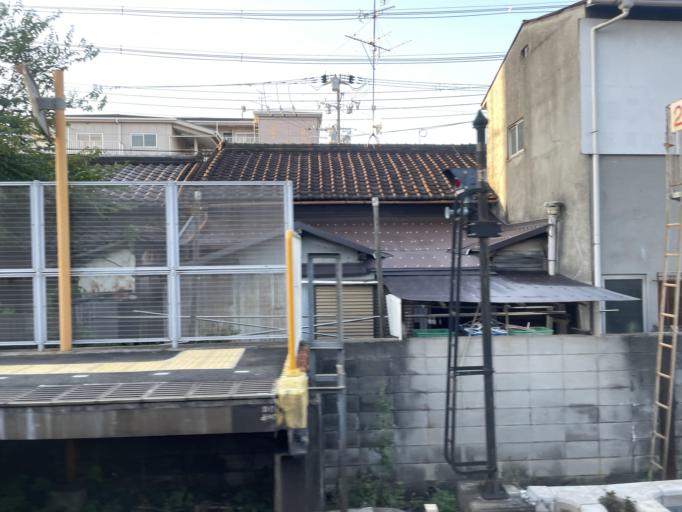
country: JP
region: Osaka
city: Matsubara
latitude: 34.5752
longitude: 135.5453
